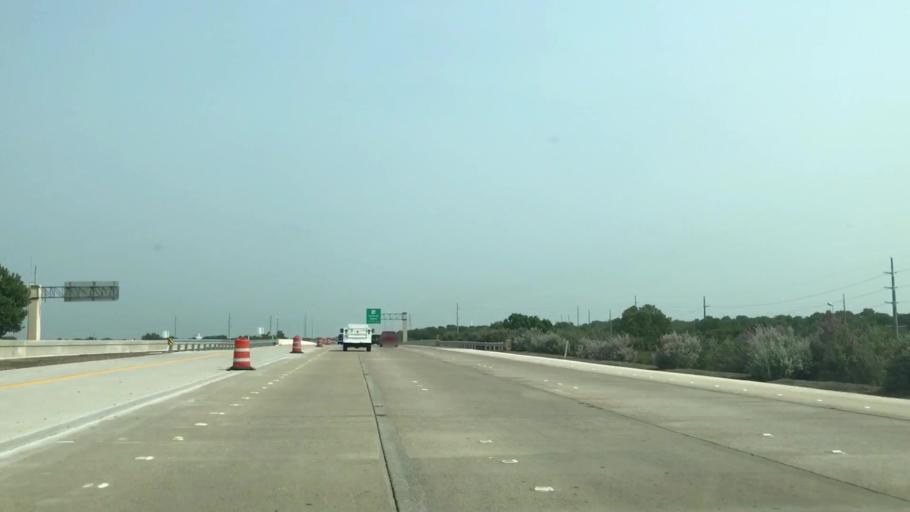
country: US
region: Texas
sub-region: Dallas County
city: Sachse
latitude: 32.9579
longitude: -96.6315
